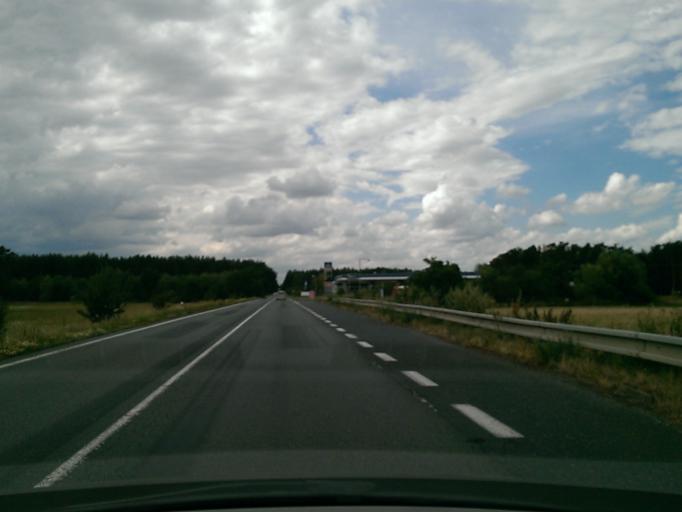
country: CZ
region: Central Bohemia
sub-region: Okres Nymburk
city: Podebrady
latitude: 50.1060
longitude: 15.1404
